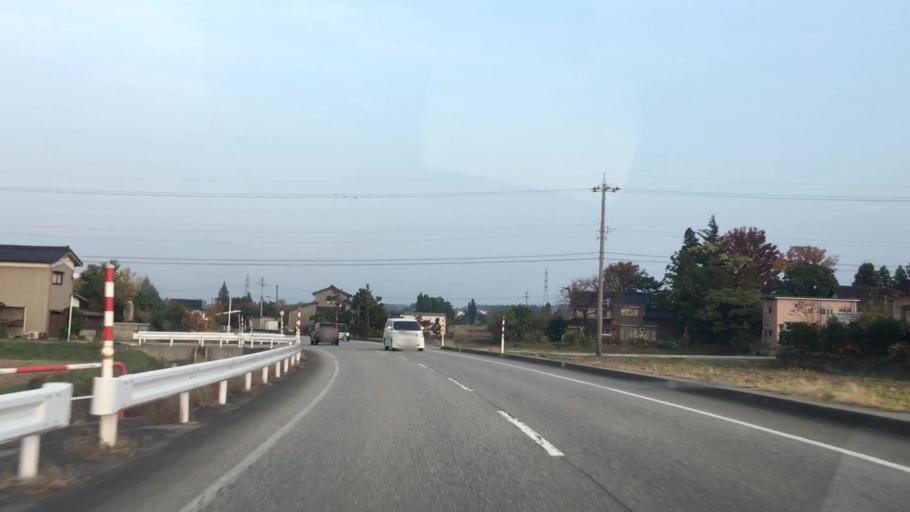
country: JP
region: Toyama
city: Yatsuomachi-higashikumisaka
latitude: 36.5992
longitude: 137.2139
